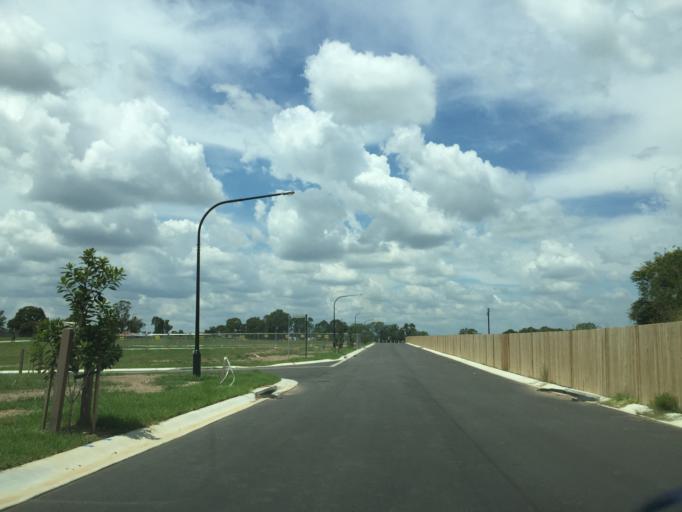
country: AU
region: New South Wales
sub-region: Blacktown
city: Riverstone
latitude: -33.6984
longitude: 150.8859
